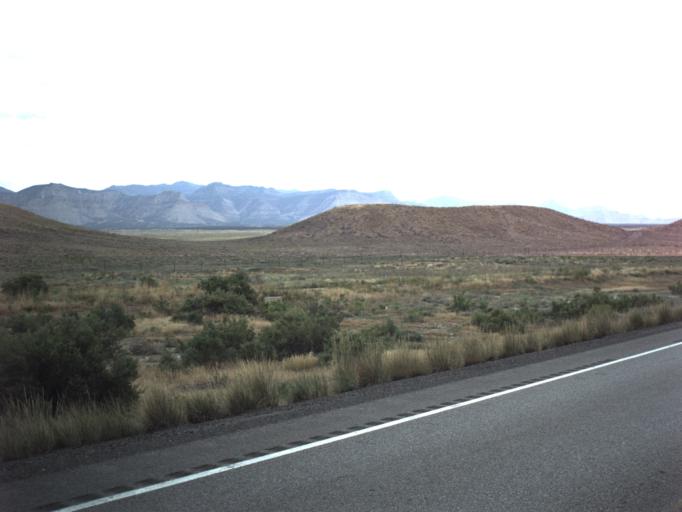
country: US
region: Utah
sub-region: Carbon County
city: East Carbon City
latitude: 39.4598
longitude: -110.4860
